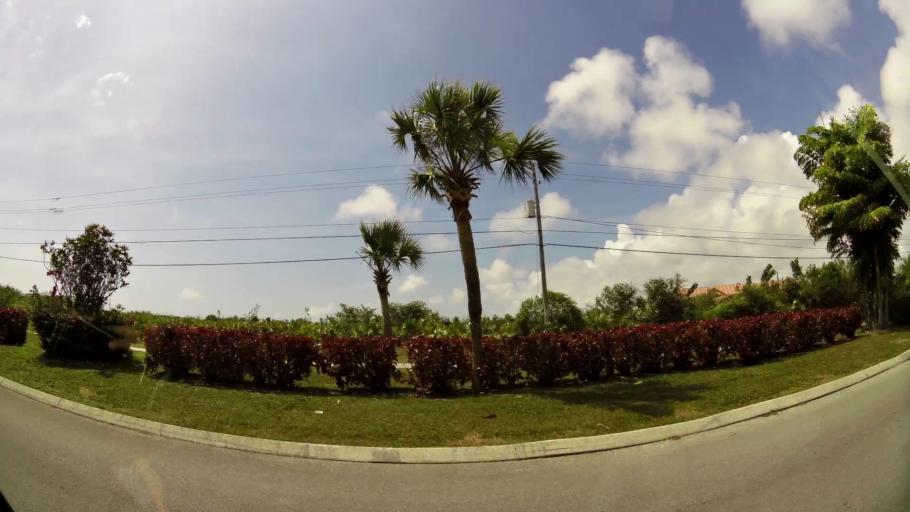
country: BS
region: Freeport
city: Freeport
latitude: 26.5090
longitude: -78.6978
